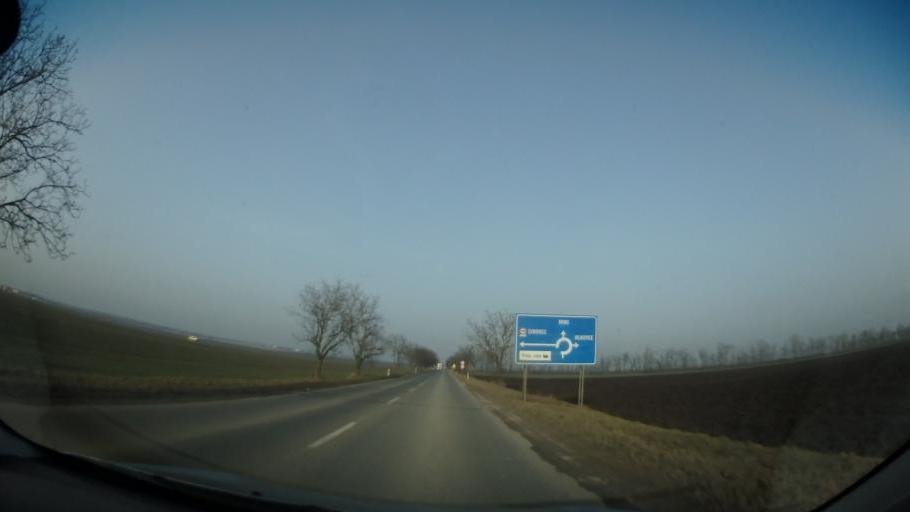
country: CZ
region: South Moravian
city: Hrusovany u Brna
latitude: 49.0649
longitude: 16.5703
